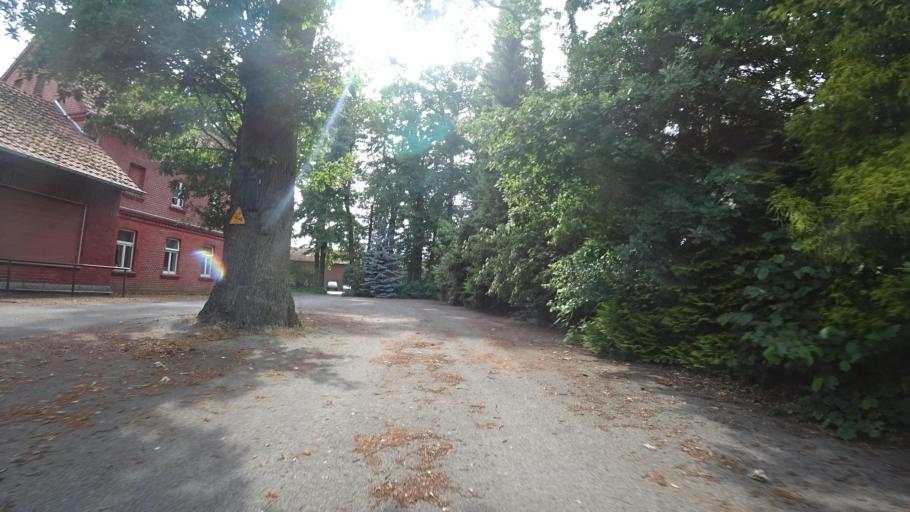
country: DE
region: North Rhine-Westphalia
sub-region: Regierungsbezirk Detmold
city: Verl
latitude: 51.9010
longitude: 8.4666
